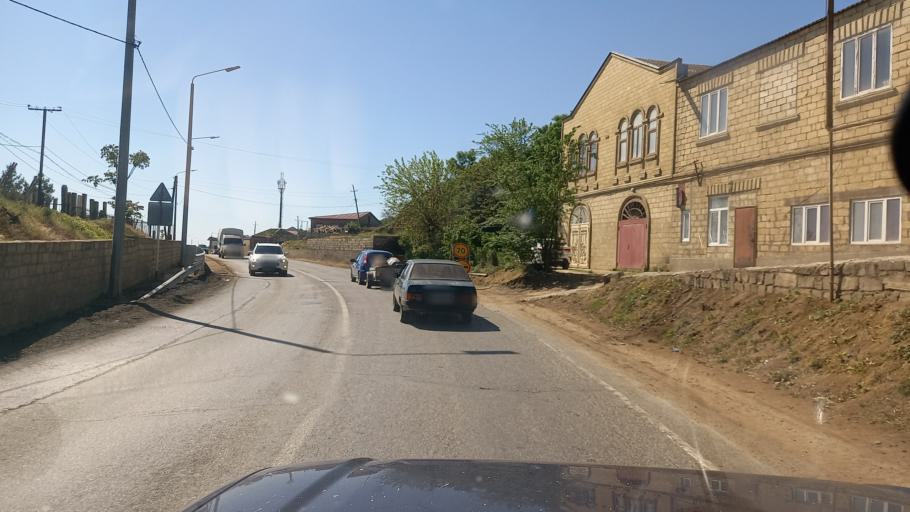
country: RU
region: Dagestan
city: Derbent
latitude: 42.0513
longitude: 48.2798
